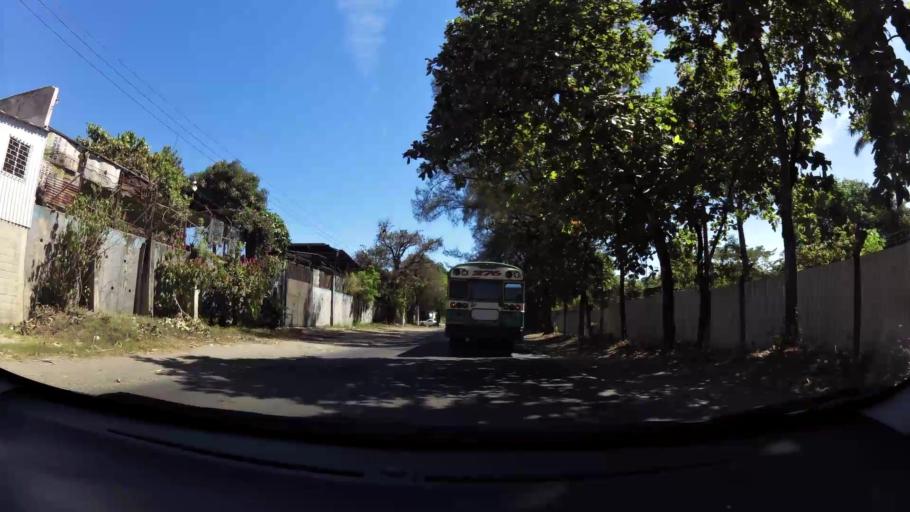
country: SV
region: San Salvador
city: Apopa
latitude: 13.8026
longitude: -89.1836
